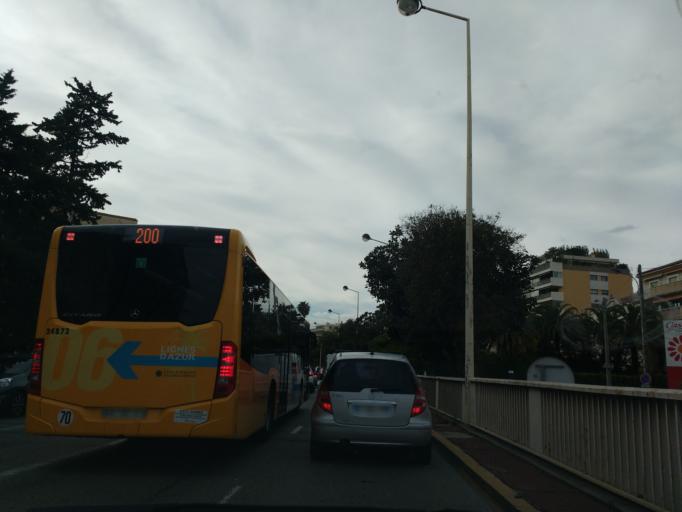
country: FR
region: Provence-Alpes-Cote d'Azur
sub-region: Departement des Alpes-Maritimes
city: Cannes
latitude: 43.5521
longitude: 7.0292
